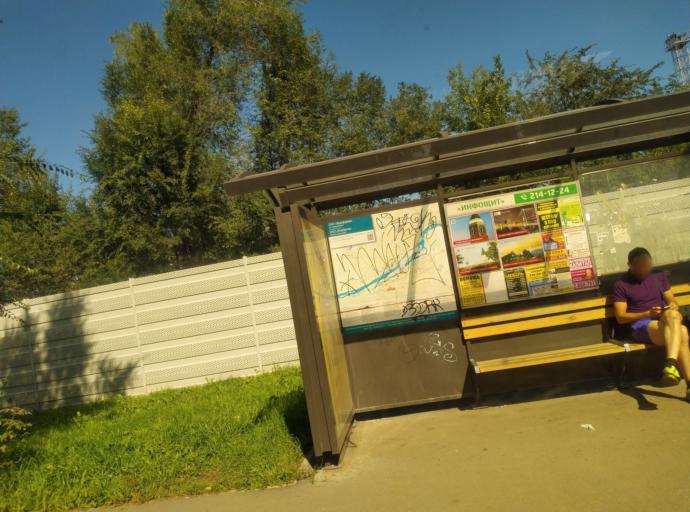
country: RU
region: Krasnoyarskiy
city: Krasnoyarsk
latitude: 55.9782
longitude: 92.8345
